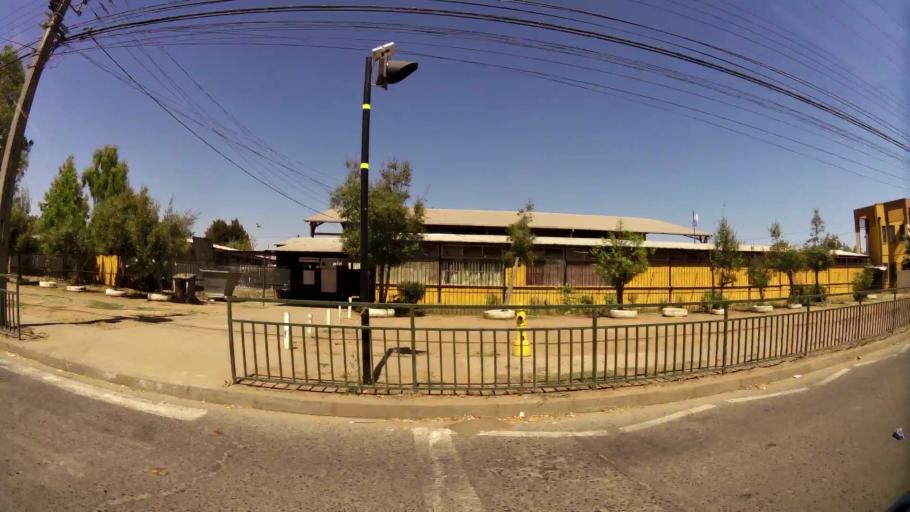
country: CL
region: Maule
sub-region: Provincia de Talca
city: Talca
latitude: -35.4125
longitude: -71.6569
